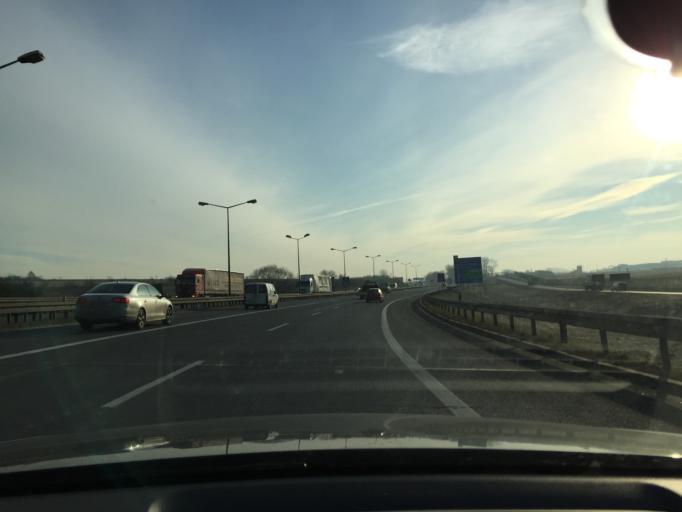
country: PL
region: Lesser Poland Voivodeship
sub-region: Powiat krakowski
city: Balice
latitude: 50.0845
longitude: 19.8079
